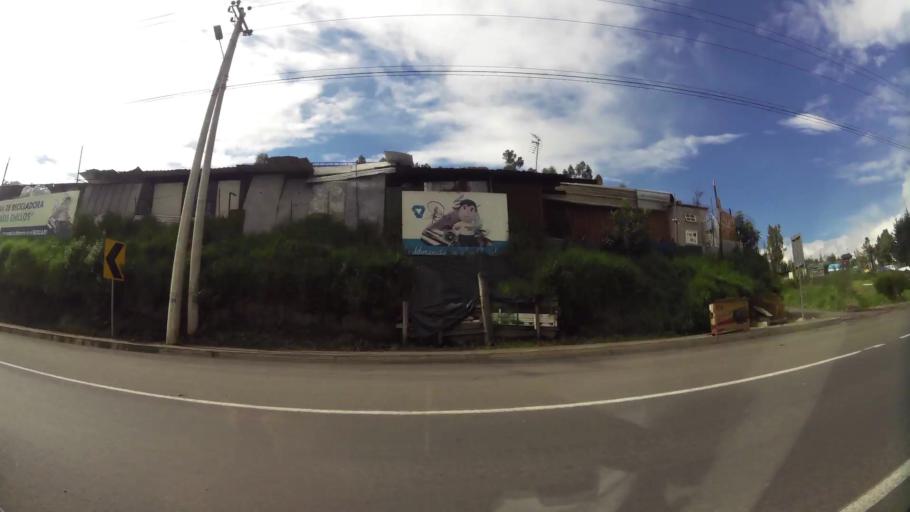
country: EC
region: Pichincha
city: Sangolqui
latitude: -0.3248
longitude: -78.4136
